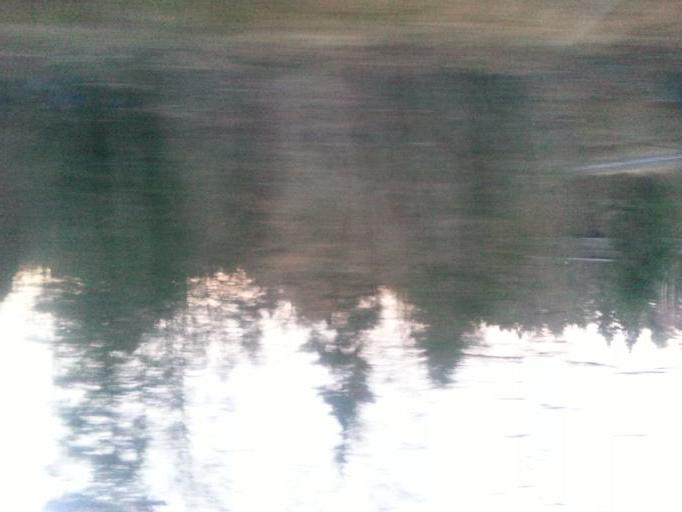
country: SE
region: Vaestra Goetaland
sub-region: Partille Kommun
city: Furulund
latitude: 57.6998
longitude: 12.1373
